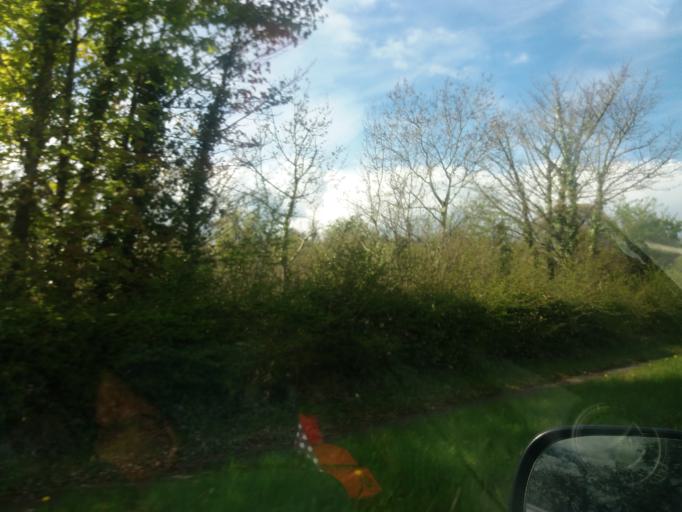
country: GB
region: Northern Ireland
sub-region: Fermanagh District
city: Enniskillen
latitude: 54.3667
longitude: -7.6796
